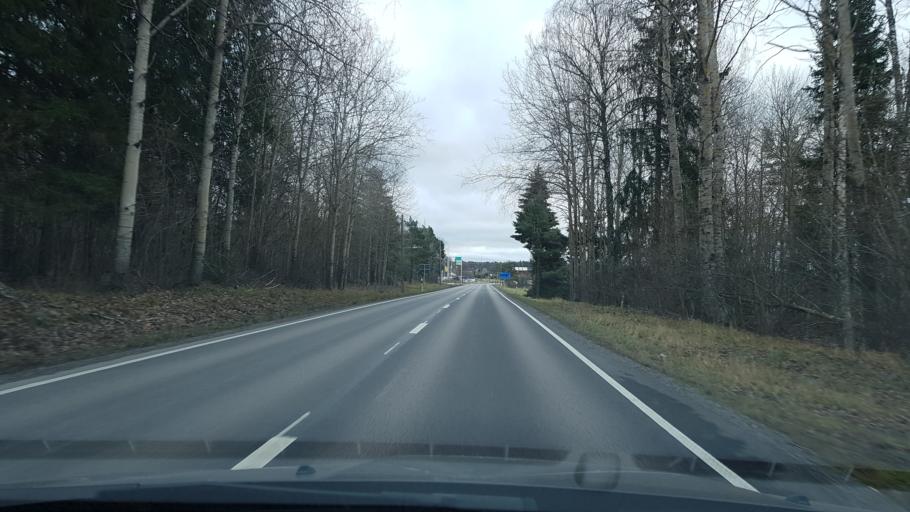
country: SE
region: Stockholm
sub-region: Norrtalje Kommun
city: Hallstavik
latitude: 60.0418
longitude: 18.5466
